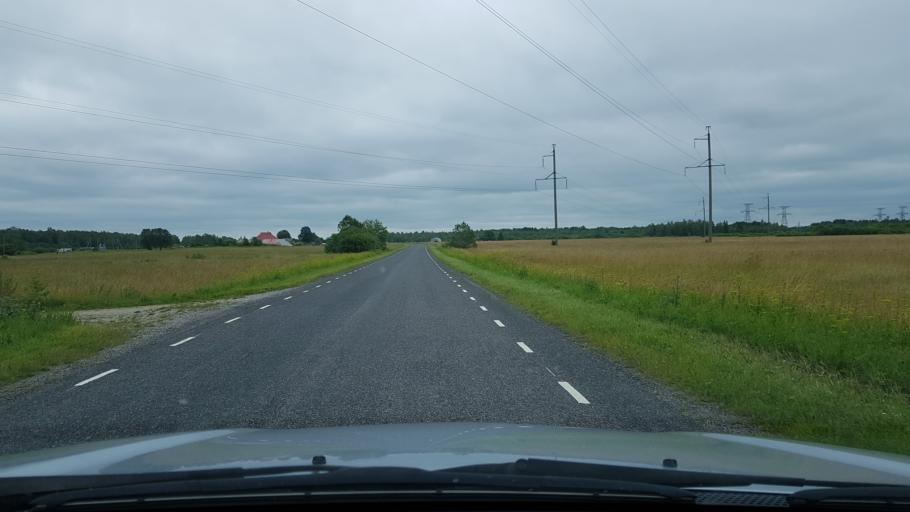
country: EE
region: Ida-Virumaa
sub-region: Narva linn
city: Narva
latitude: 59.3715
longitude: 28.0978
